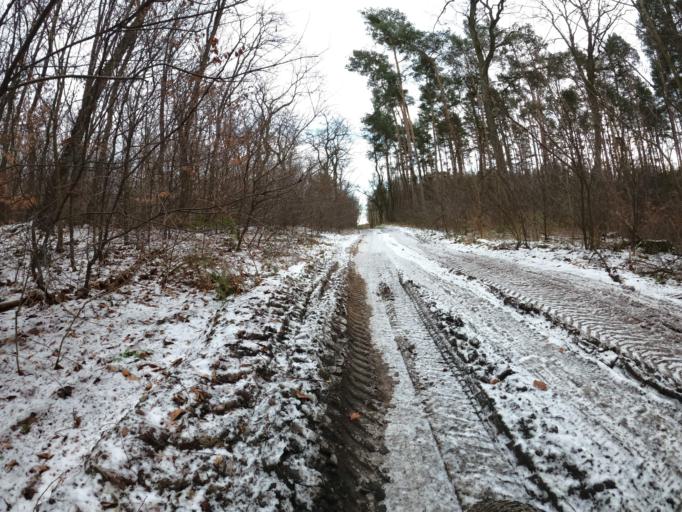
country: PL
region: Lubusz
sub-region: Powiat slubicki
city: Cybinka
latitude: 52.2030
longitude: 14.8555
